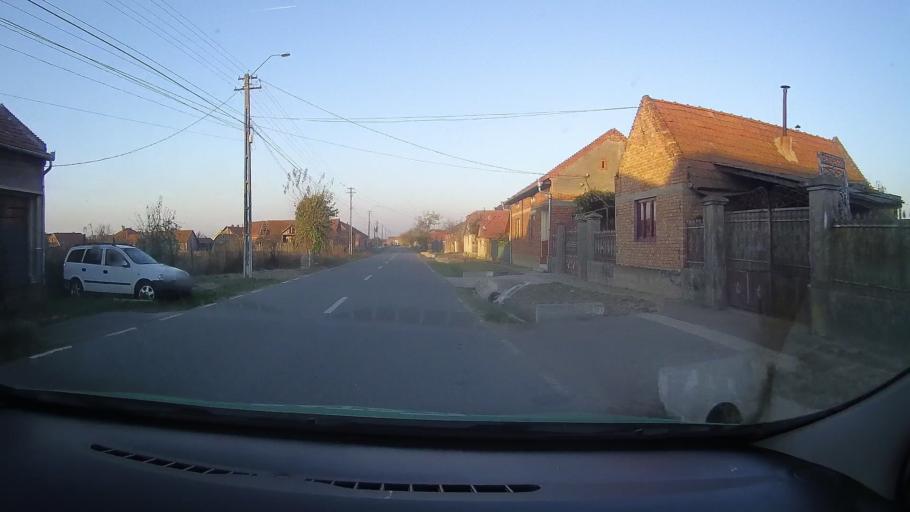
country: RO
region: Timis
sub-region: Comuna Traian Vuia
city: Traian Vuia
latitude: 45.8018
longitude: 22.0243
